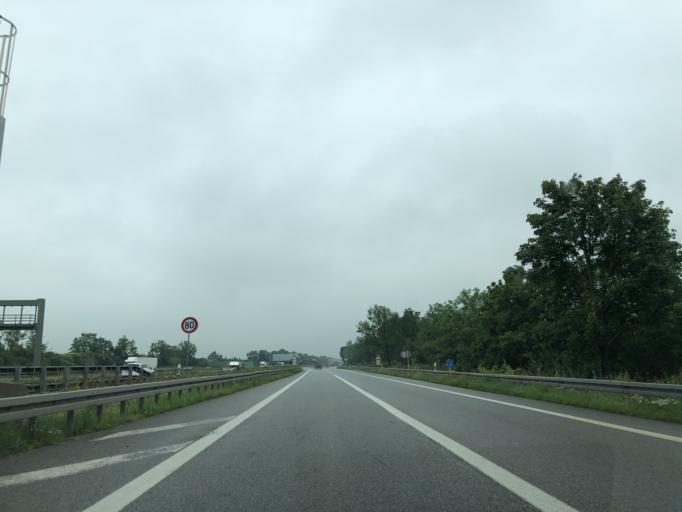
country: DE
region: Bavaria
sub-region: Upper Bavaria
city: Feldkirchen
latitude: 48.1410
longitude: 11.7578
